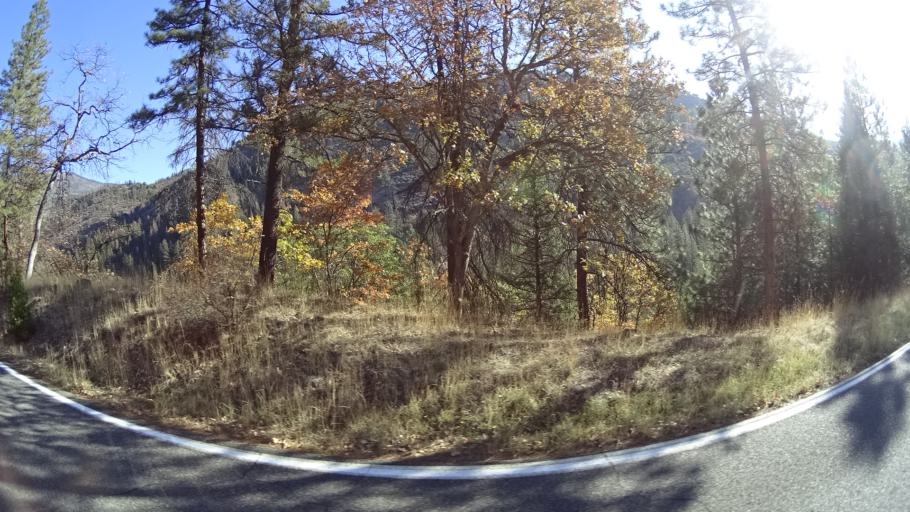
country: US
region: California
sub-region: Siskiyou County
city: Yreka
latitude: 41.8849
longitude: -122.8235
